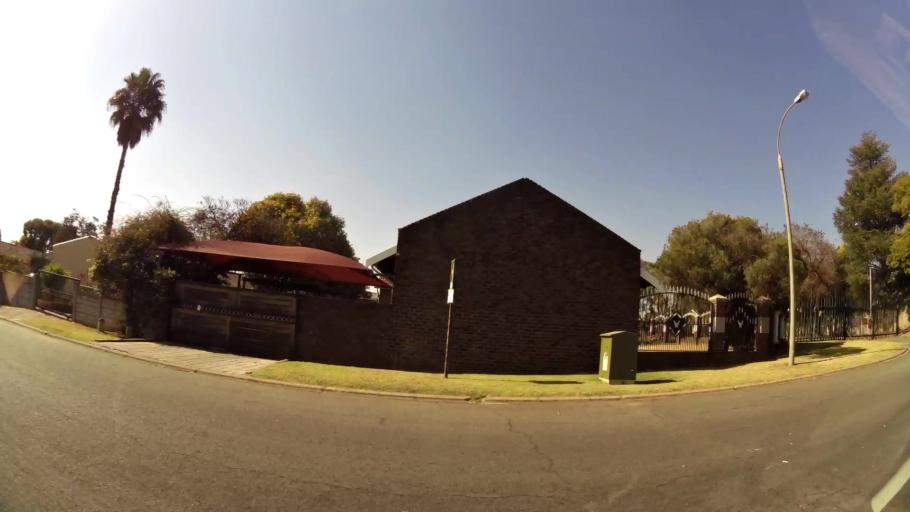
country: ZA
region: Gauteng
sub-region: Ekurhuleni Metropolitan Municipality
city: Tembisa
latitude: -26.0434
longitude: 28.2305
